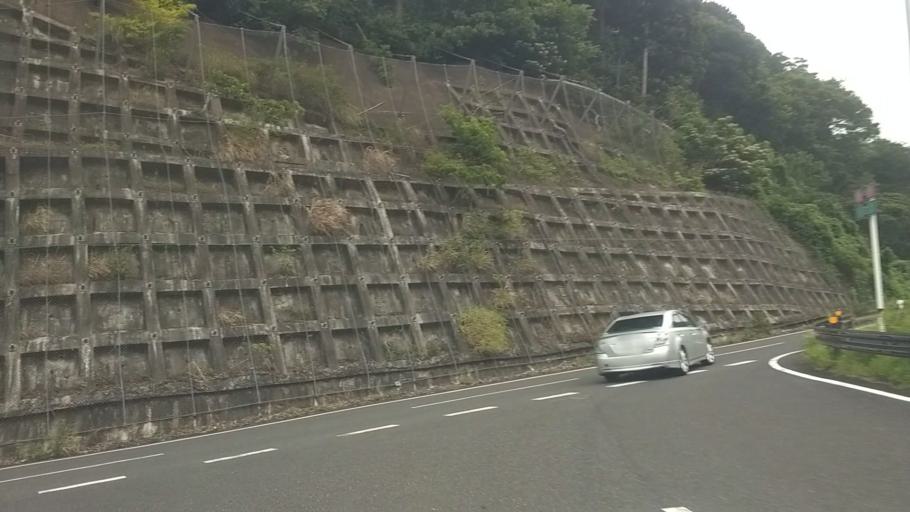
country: JP
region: Chiba
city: Kawaguchi
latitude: 35.2188
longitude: 140.1389
